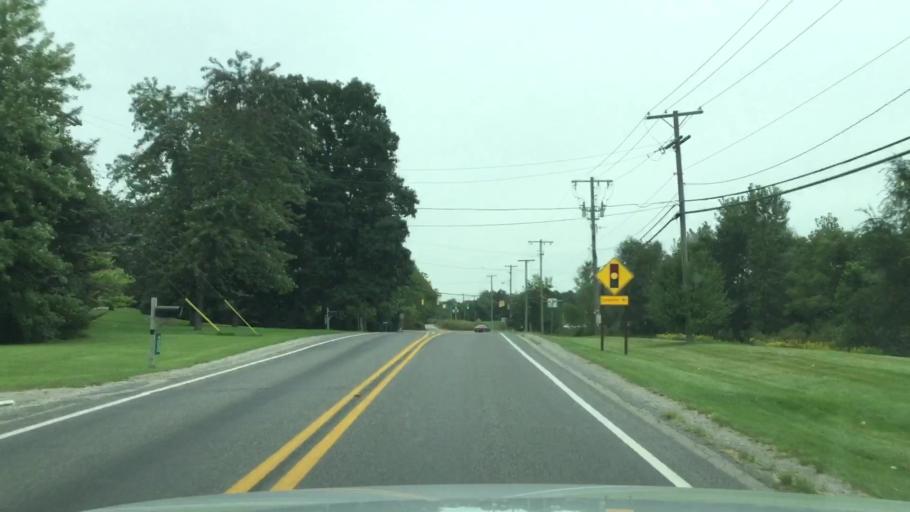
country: US
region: Michigan
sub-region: Washtenaw County
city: Ypsilanti
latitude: 42.2013
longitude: -83.6770
